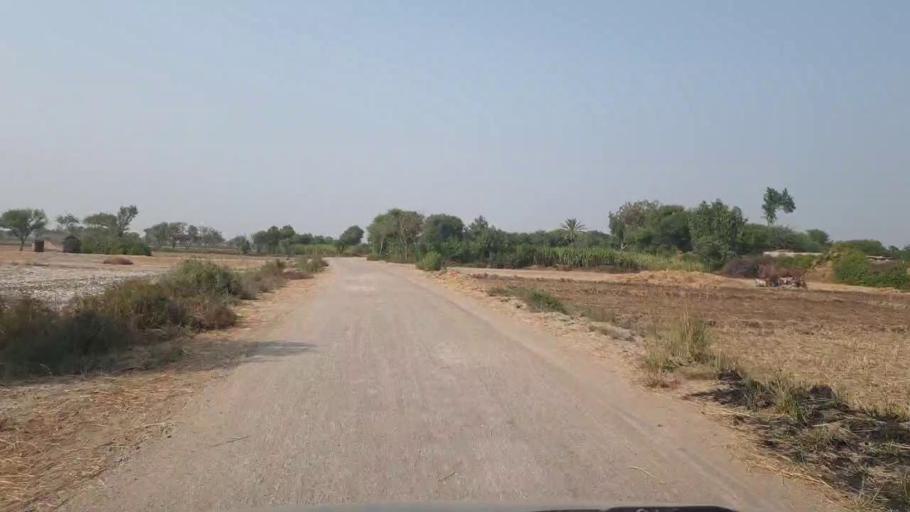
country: PK
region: Sindh
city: Tando Muhammad Khan
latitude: 25.0832
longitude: 68.3416
